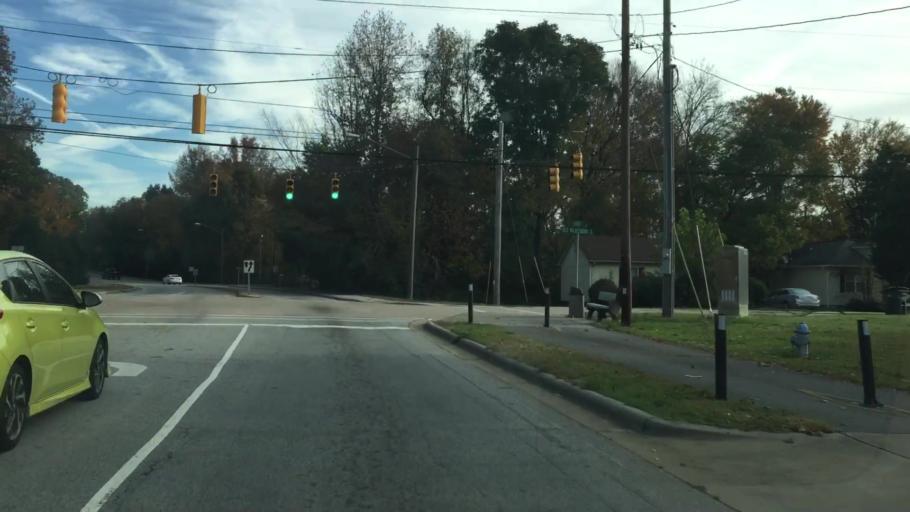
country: US
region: North Carolina
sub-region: Rowan County
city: Salisbury
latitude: 35.6757
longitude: -80.4904
